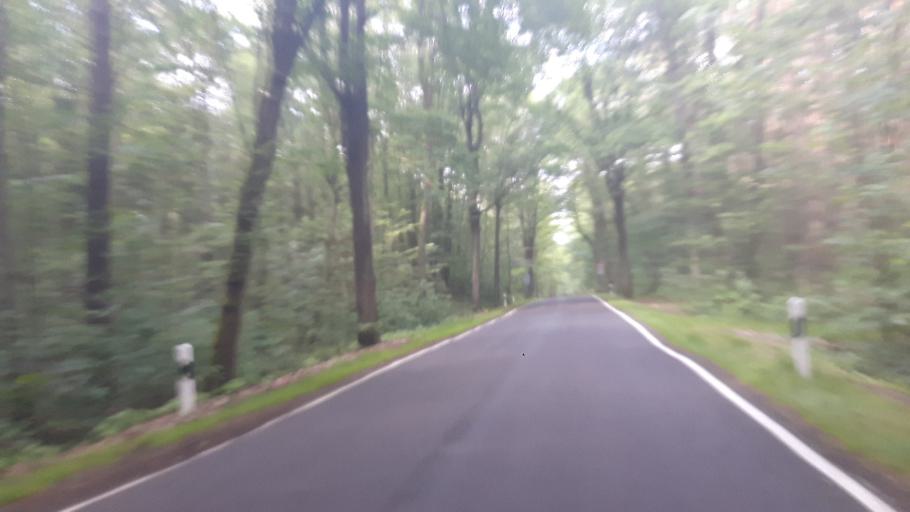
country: DE
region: Brandenburg
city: Hohenfinow
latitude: 52.7885
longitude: 13.9000
